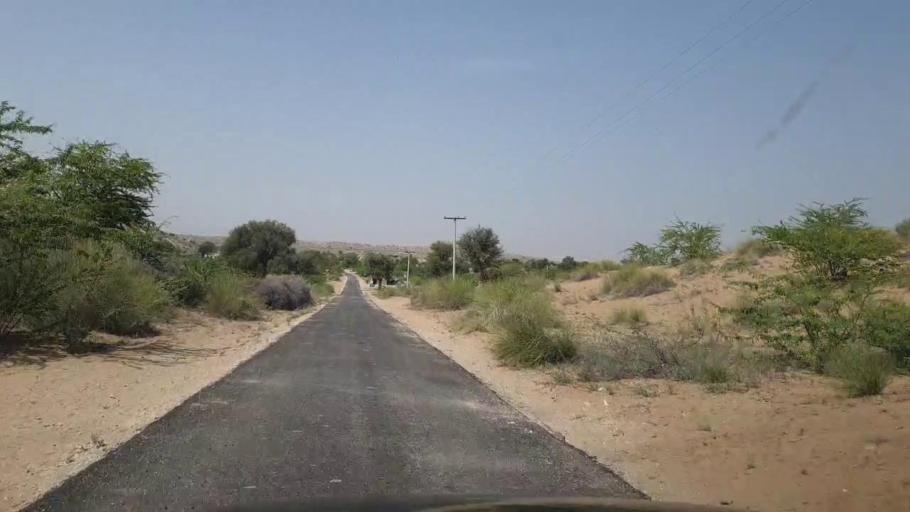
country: PK
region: Sindh
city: Islamkot
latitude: 25.1065
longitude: 70.6534
